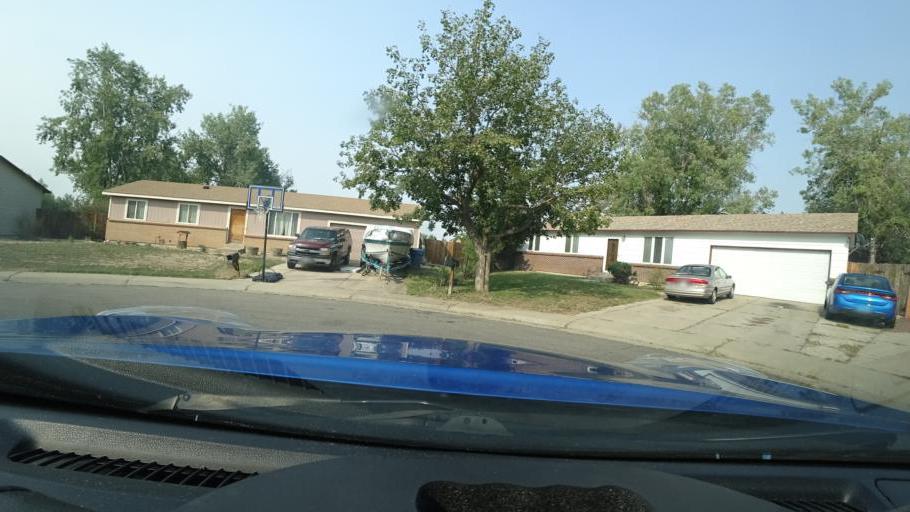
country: US
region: Colorado
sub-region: Adams County
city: Aurora
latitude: 39.6653
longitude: -104.7997
